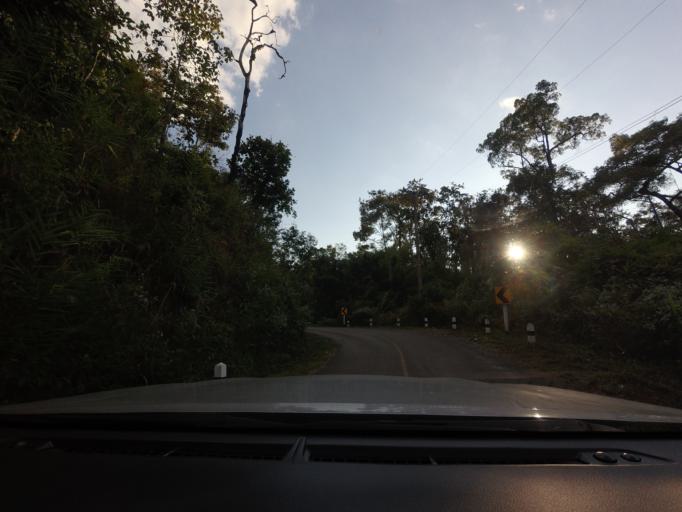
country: TH
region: Chiang Mai
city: Phrao
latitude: 19.4894
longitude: 99.1673
